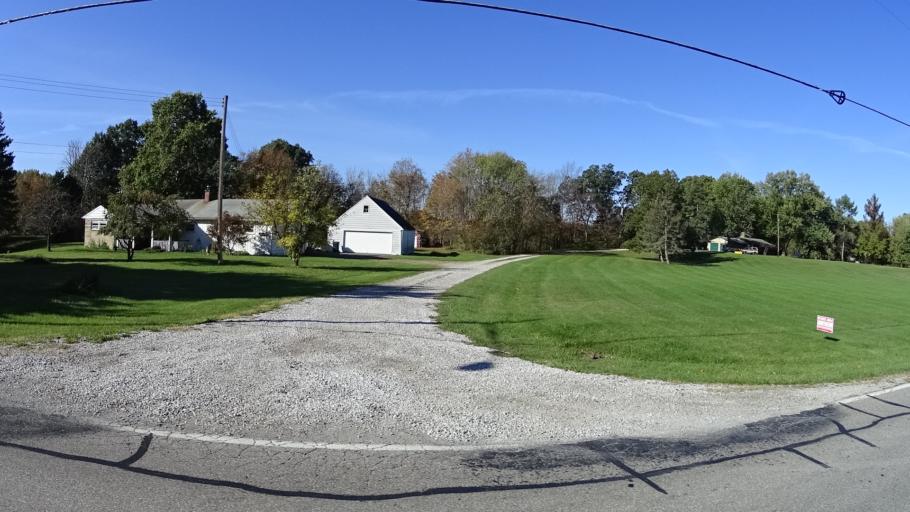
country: US
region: Ohio
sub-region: Lorain County
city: Vermilion-on-the-Lake
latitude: 41.3959
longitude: -82.3250
